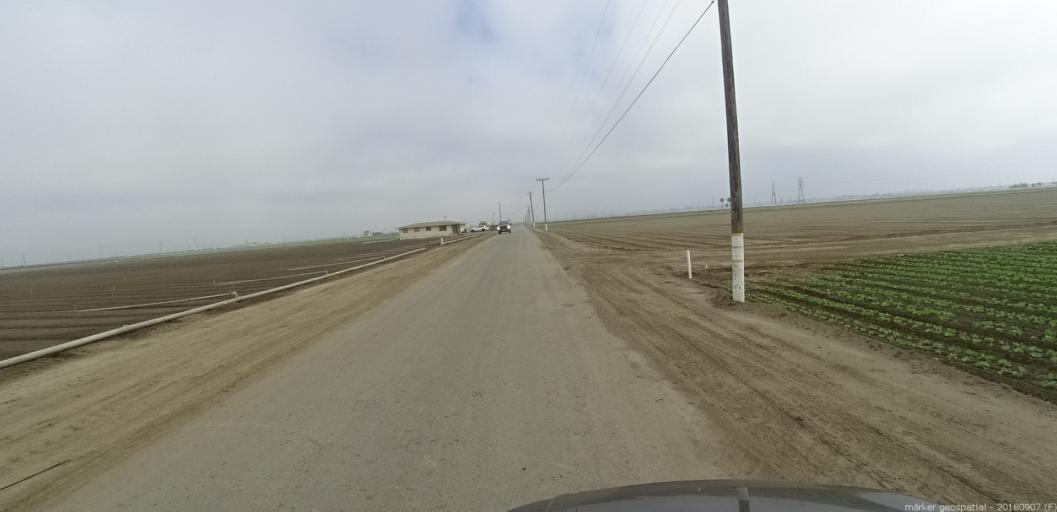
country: US
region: California
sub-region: Monterey County
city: Boronda
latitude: 36.6694
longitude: -121.7056
